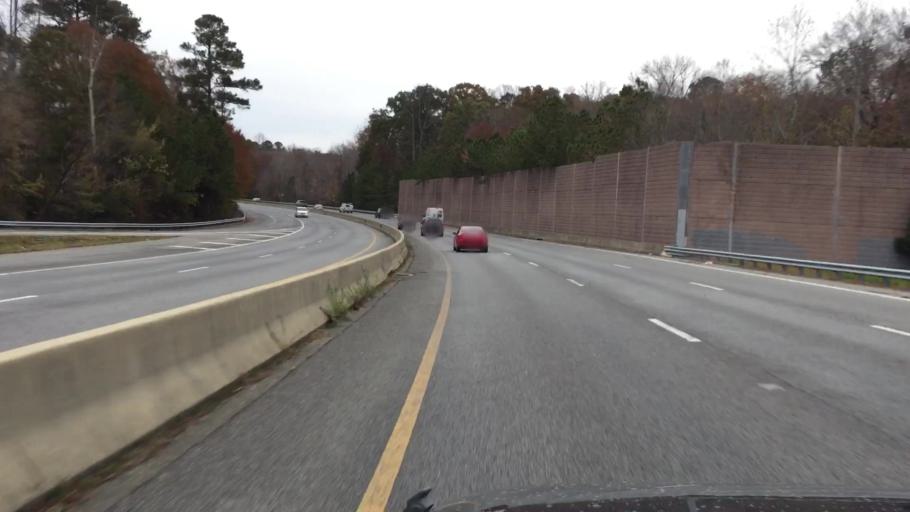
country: US
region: Virginia
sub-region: James City County
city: Williamsburg
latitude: 37.3004
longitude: -76.7444
